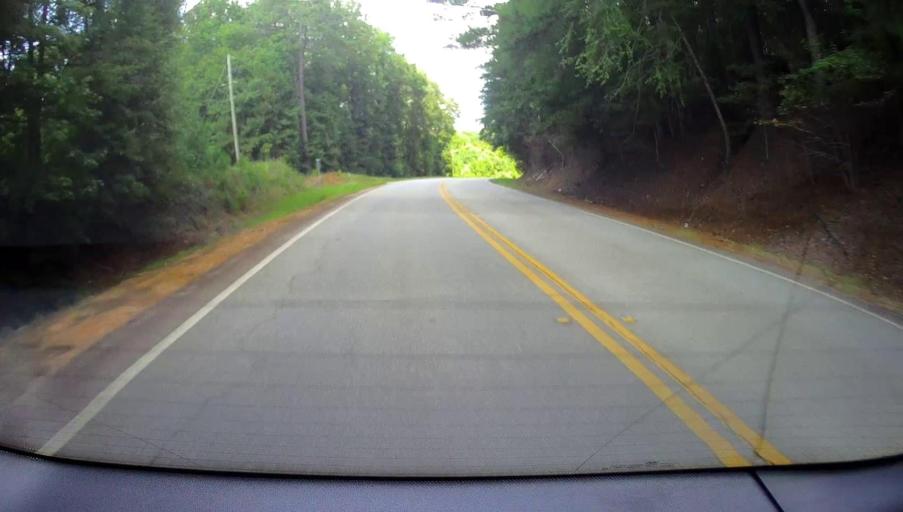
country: US
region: Georgia
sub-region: Crawford County
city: Knoxville
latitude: 32.8814
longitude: -84.0259
